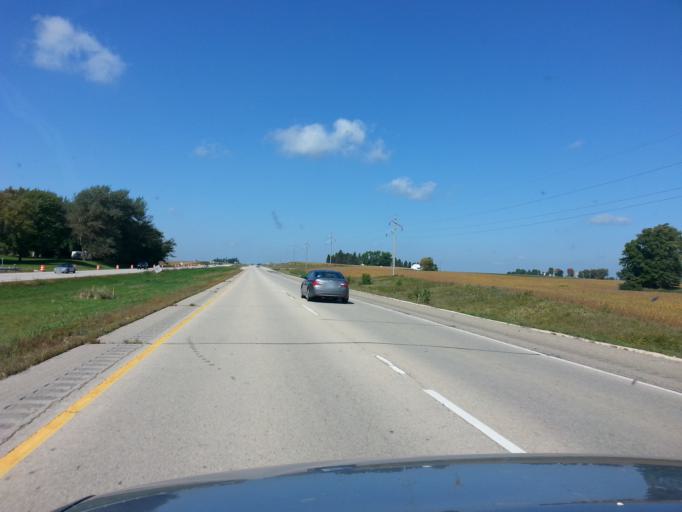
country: US
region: Minnesota
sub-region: Goodhue County
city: Wanamingo
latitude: 44.4024
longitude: -92.8480
